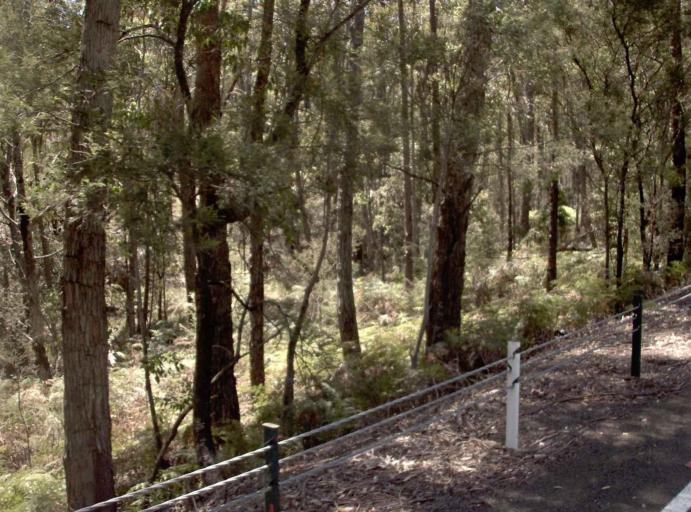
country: AU
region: Victoria
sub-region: East Gippsland
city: Lakes Entrance
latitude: -37.7308
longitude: 148.1153
